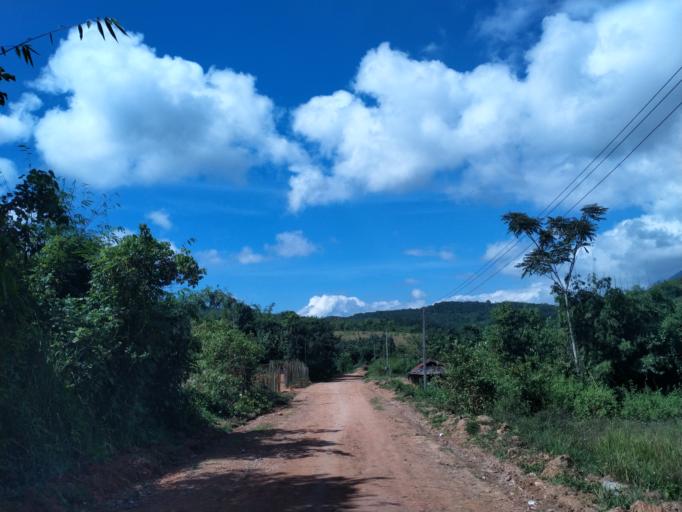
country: TH
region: Nong Khai
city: Rattanawapi
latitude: 18.6380
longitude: 102.9513
